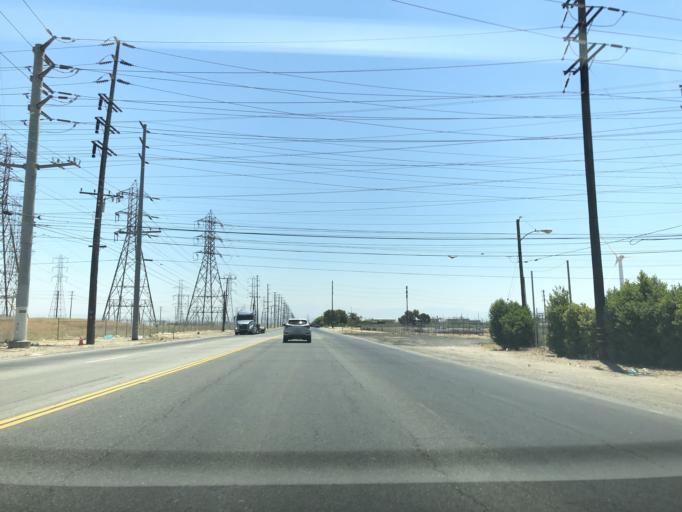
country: US
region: California
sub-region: San Bernardino County
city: Rancho Cucamonga
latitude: 34.0887
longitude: -117.5239
